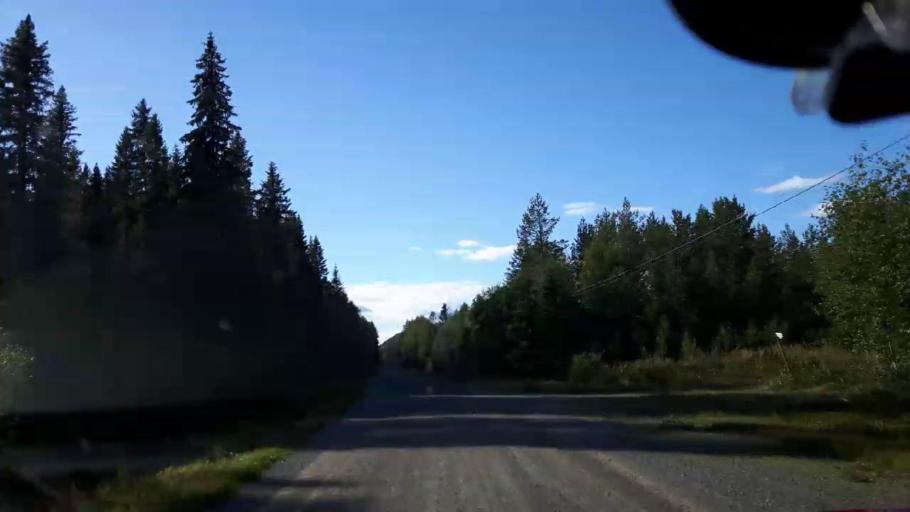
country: SE
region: Jaemtland
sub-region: Ragunda Kommun
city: Hammarstrand
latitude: 63.4849
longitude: 16.1093
